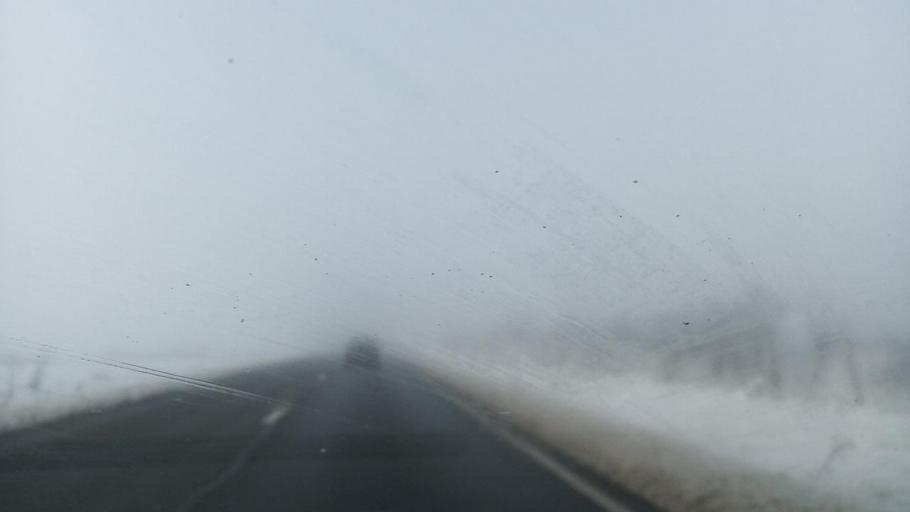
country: RO
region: Suceava
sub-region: Municipiul Falticeni
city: Falticeni
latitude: 47.4374
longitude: 26.2851
